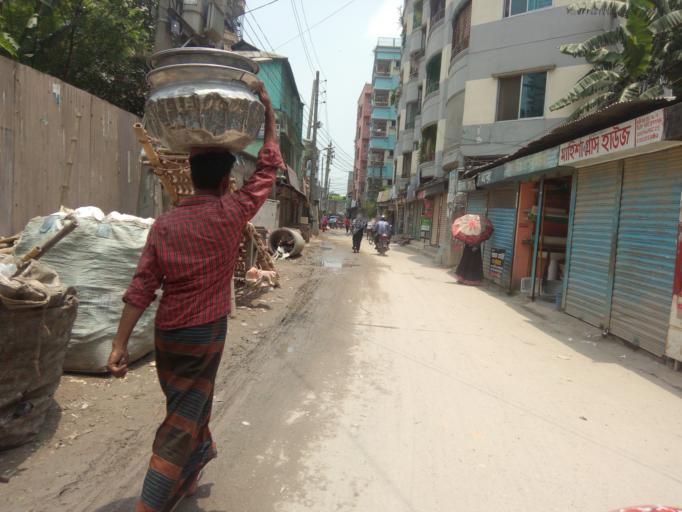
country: BD
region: Dhaka
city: Paltan
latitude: 23.7606
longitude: 90.4318
